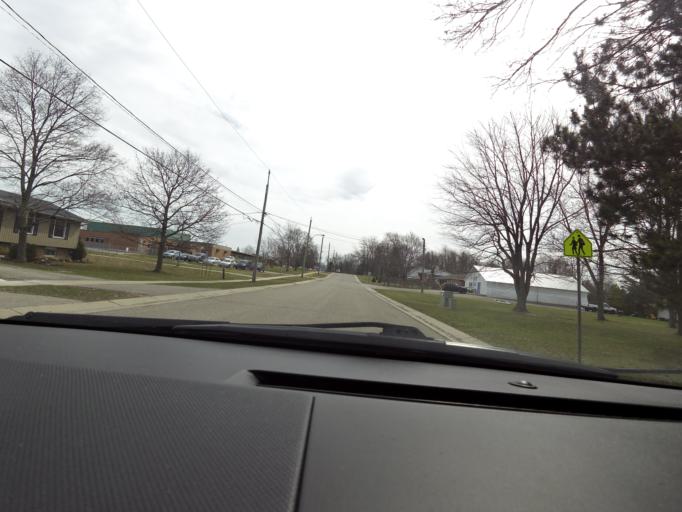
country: CA
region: Ontario
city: Ancaster
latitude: 42.9456
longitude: -79.8537
